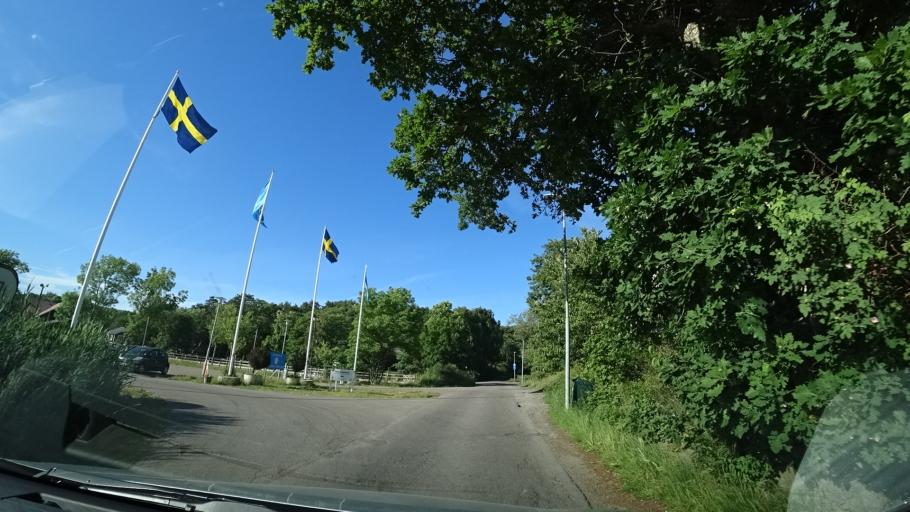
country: SE
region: Vaestra Goetaland
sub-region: Goteborg
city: Billdal
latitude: 57.5796
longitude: 11.9465
